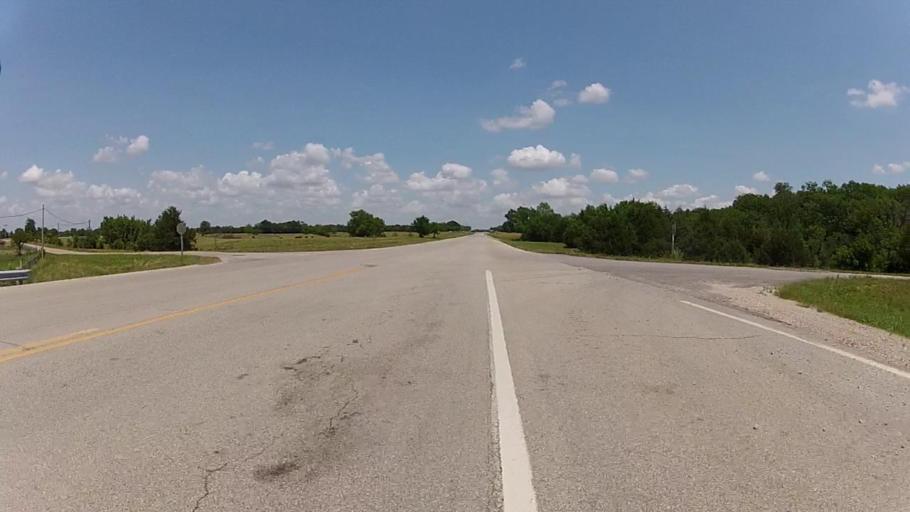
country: US
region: Kansas
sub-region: Labette County
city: Altamont
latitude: 37.1928
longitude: -95.4142
